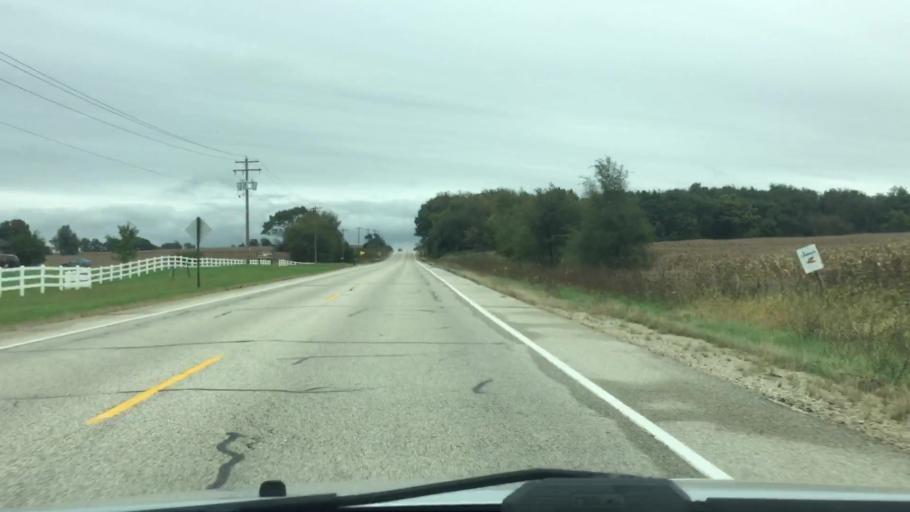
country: US
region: Wisconsin
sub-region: Jefferson County
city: Palmyra
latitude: 42.8137
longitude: -88.5624
